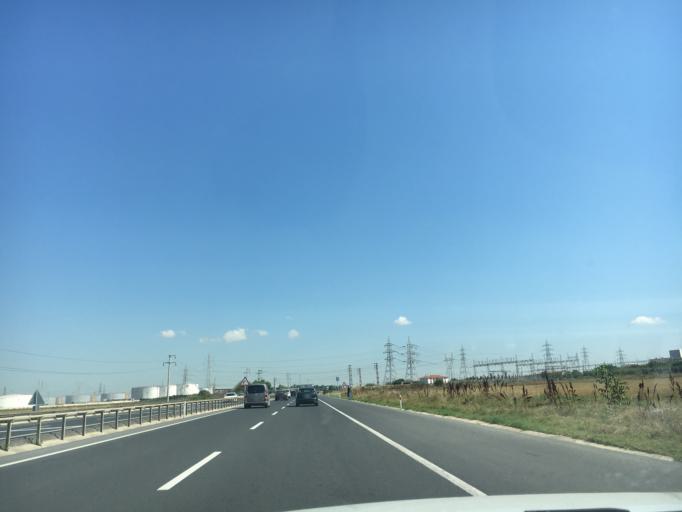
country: TR
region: Tekirdag
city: Marmara Ereglisi
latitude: 40.9909
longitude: 27.9725
